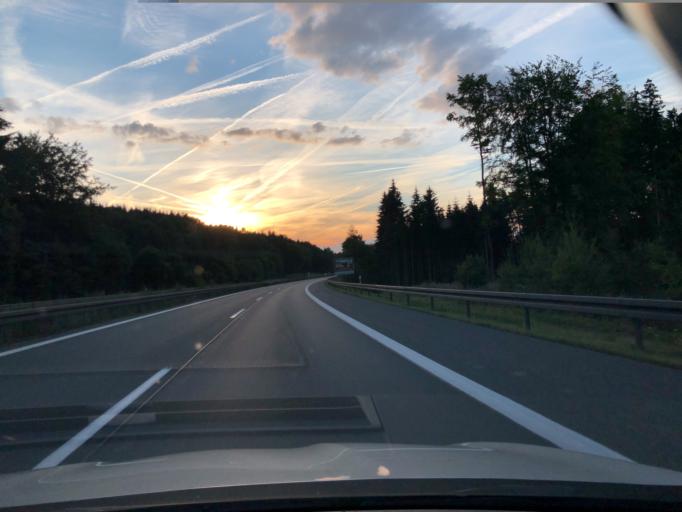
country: DE
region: Bavaria
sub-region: Regierungsbezirk Mittelfranken
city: Alfeld
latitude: 49.4079
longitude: 11.5785
